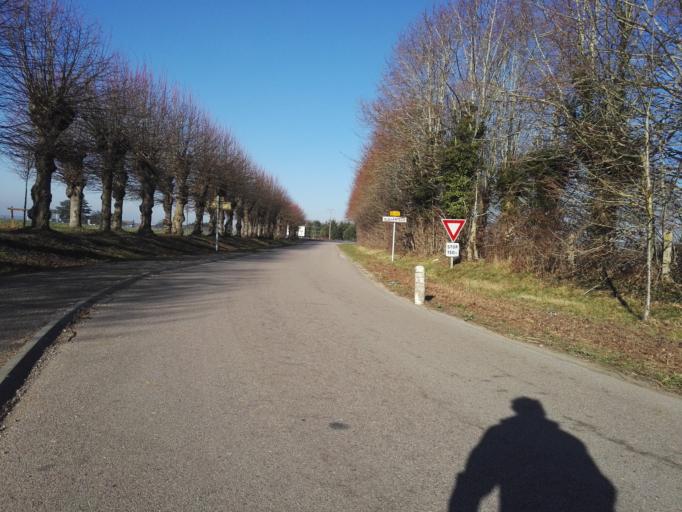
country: FR
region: Haute-Normandie
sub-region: Departement de l'Eure
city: Pacy-sur-Eure
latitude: 49.0086
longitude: 1.4167
